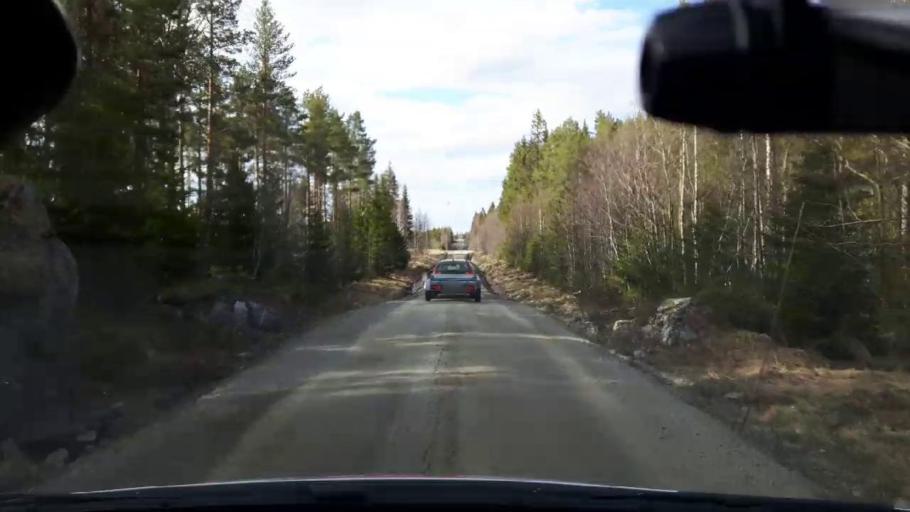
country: SE
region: Jaemtland
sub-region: Bergs Kommun
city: Hoverberg
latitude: 62.8517
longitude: 14.6703
